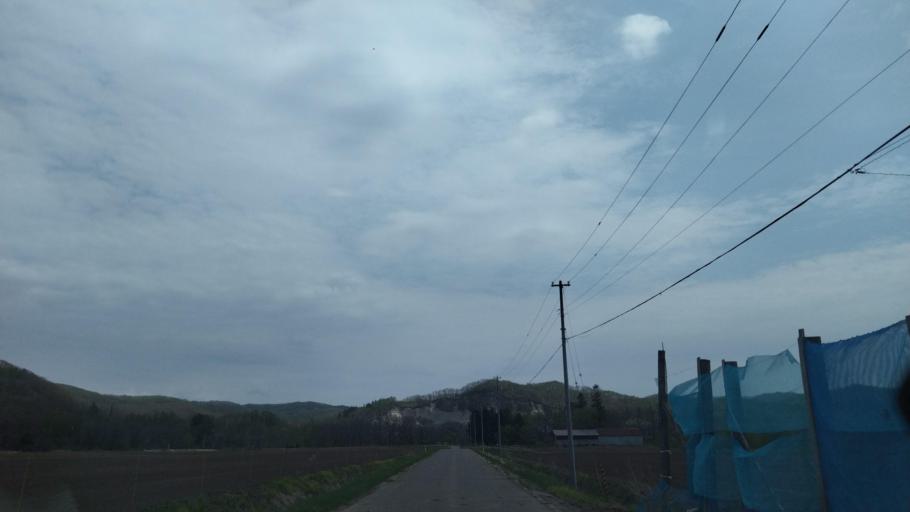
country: JP
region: Hokkaido
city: Otofuke
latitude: 43.3158
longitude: 143.5734
